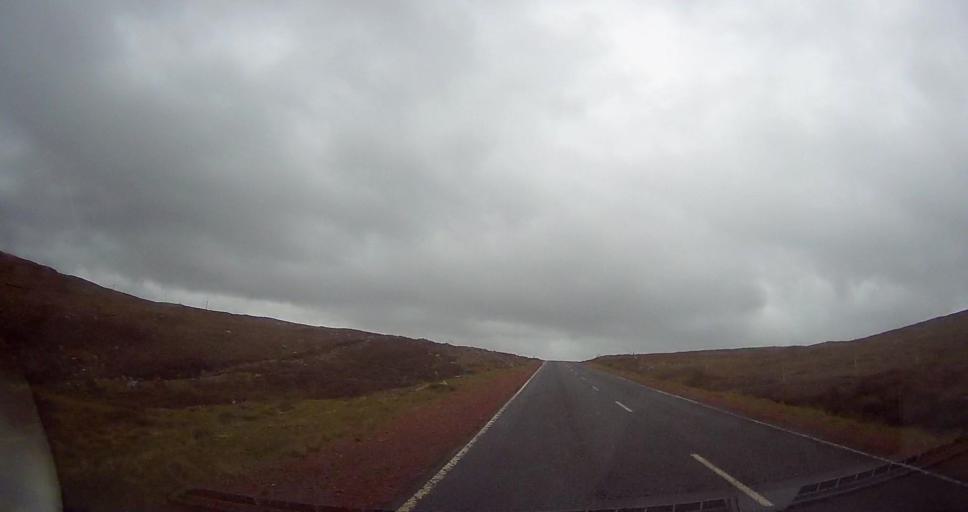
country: GB
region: Scotland
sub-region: Shetland Islands
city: Lerwick
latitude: 60.4852
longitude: -1.4480
